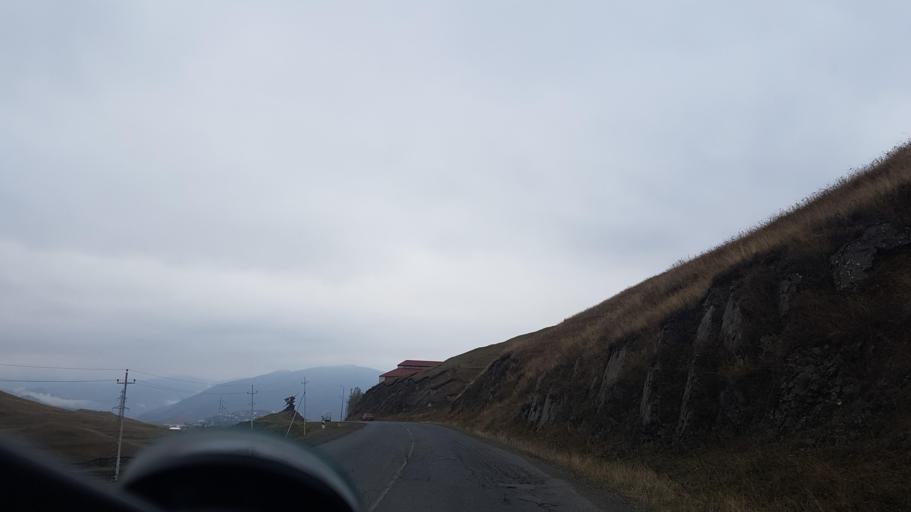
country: AZ
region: Gadabay Rayon
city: Ariqdam
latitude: 40.6156
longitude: 45.8104
